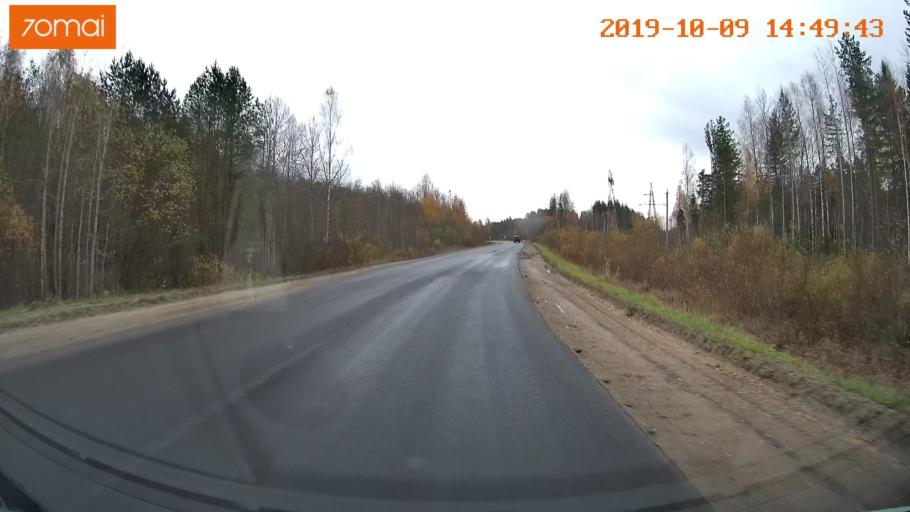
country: RU
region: Kostroma
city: Chistyye Bory
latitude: 58.3905
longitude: 41.5868
